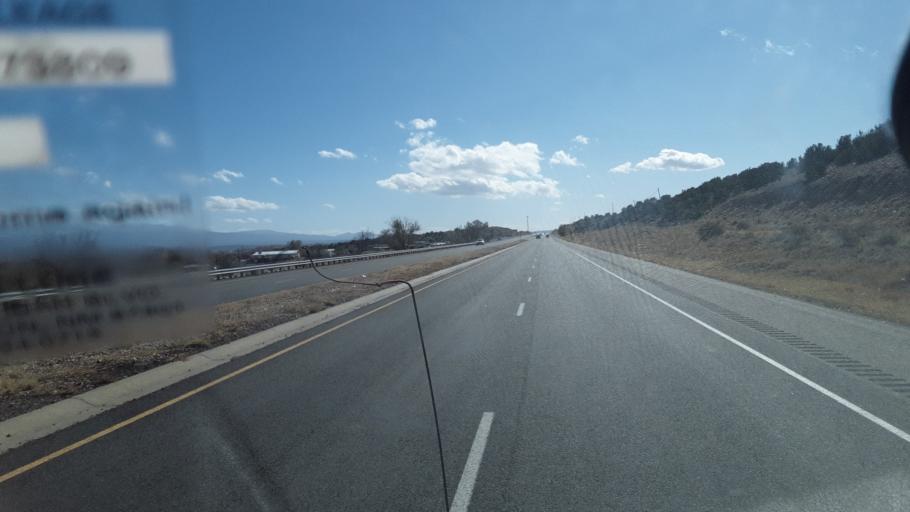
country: US
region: New Mexico
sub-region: Rio Arriba County
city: Ohkay Owingeh
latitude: 36.0336
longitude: -106.0946
